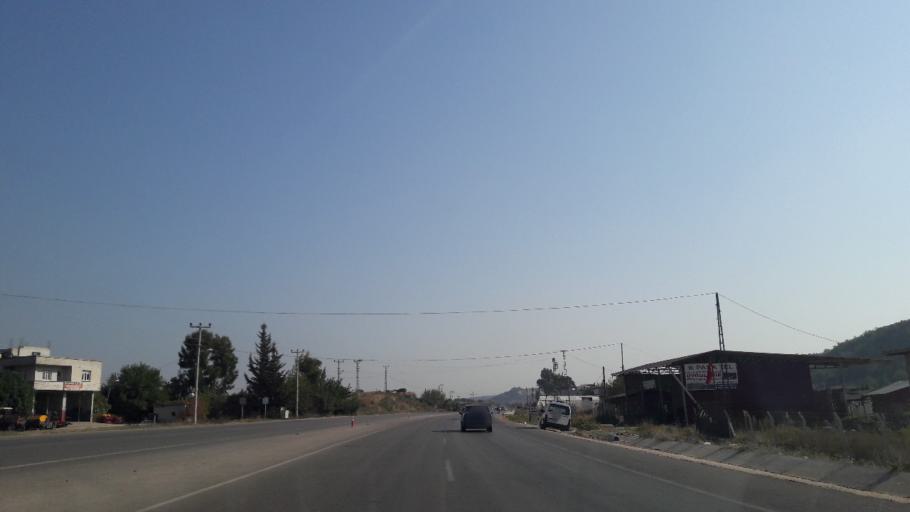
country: TR
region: Adana
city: Yuregir
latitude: 37.0651
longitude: 35.4479
